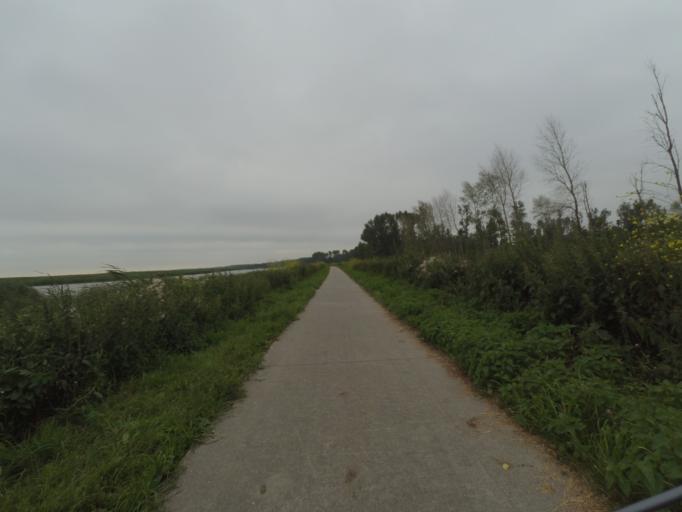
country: NL
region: Flevoland
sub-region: Gemeente Almere
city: Almere Stad
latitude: 52.4293
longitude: 5.2660
